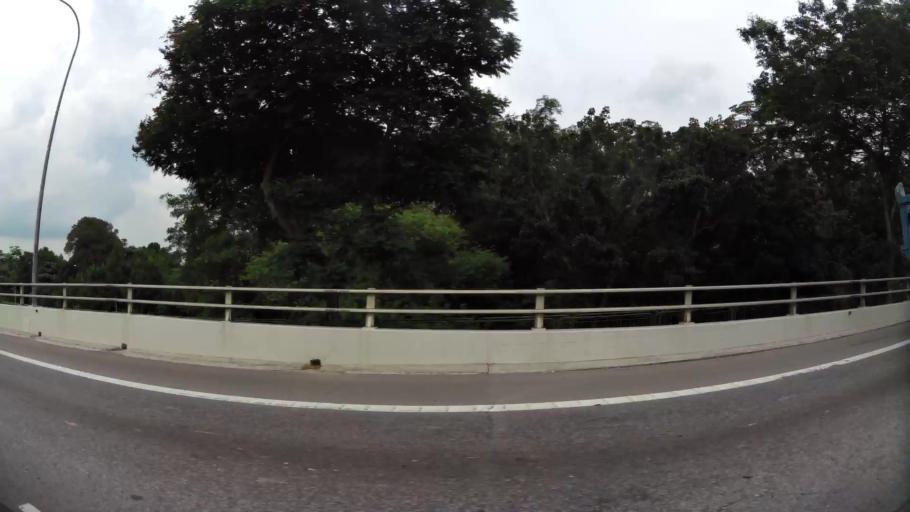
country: MY
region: Johor
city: Johor Bahru
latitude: 1.4016
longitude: 103.8125
